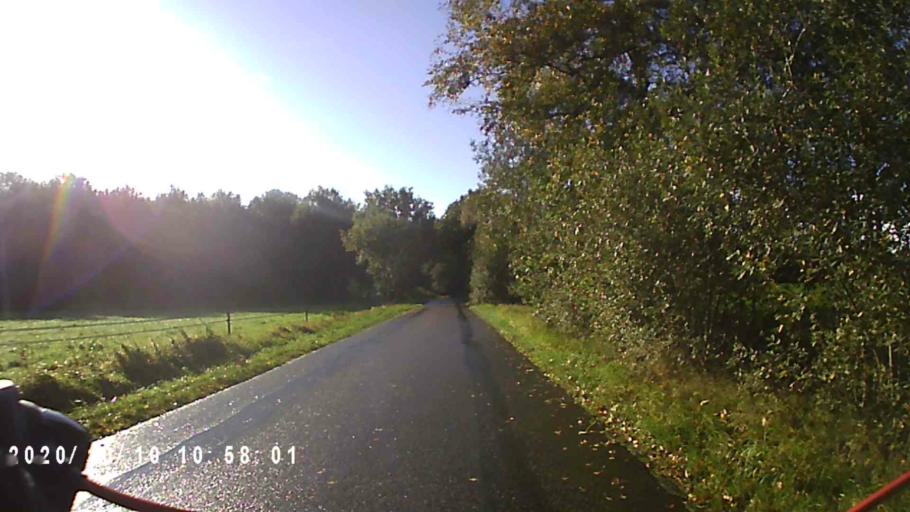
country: NL
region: Friesland
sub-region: Gemeente Achtkarspelen
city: Surhuisterveen
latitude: 53.1463
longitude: 6.2064
